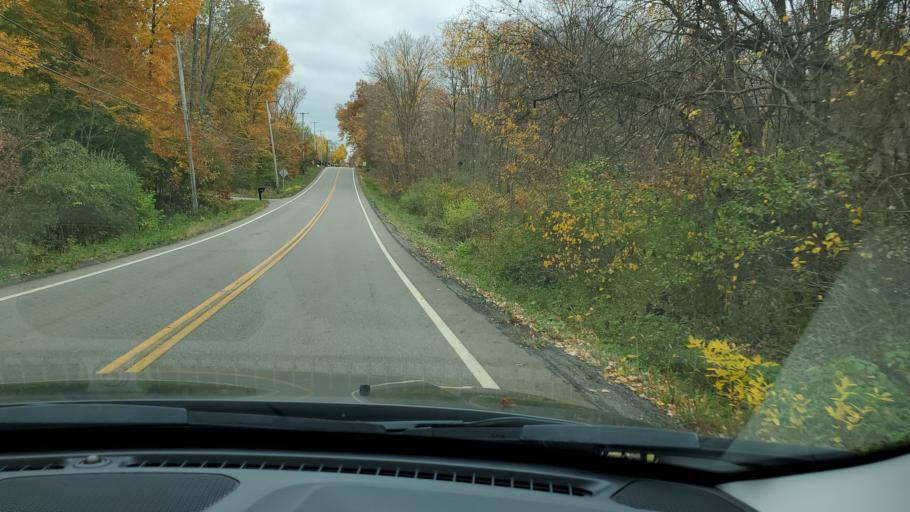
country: US
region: Ohio
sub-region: Mahoning County
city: Boardman
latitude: 40.9790
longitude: -80.6532
